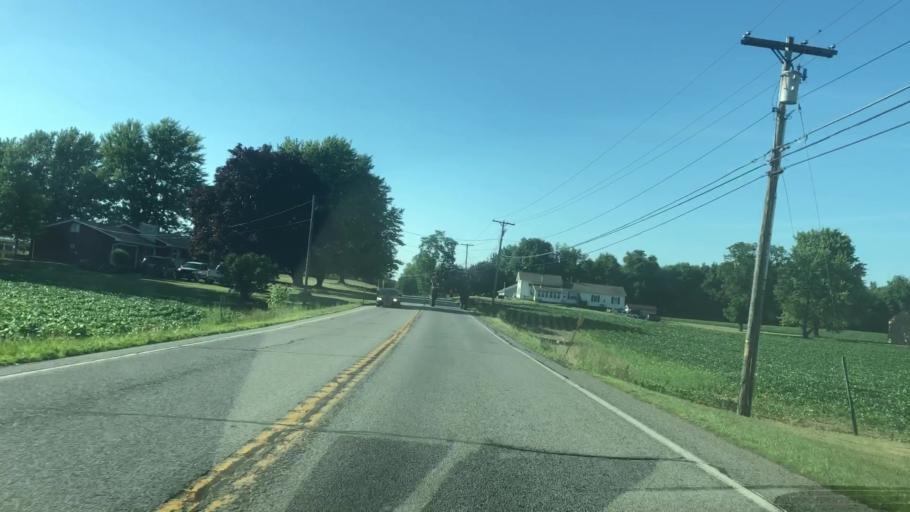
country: US
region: New York
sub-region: Wayne County
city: Ontario
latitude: 43.1909
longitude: -77.2922
